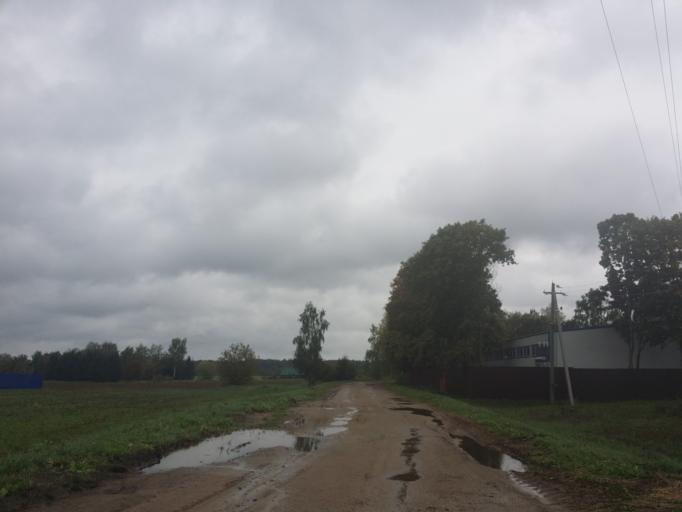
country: BY
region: Minsk
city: Chervyen'
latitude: 53.7641
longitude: 28.2516
